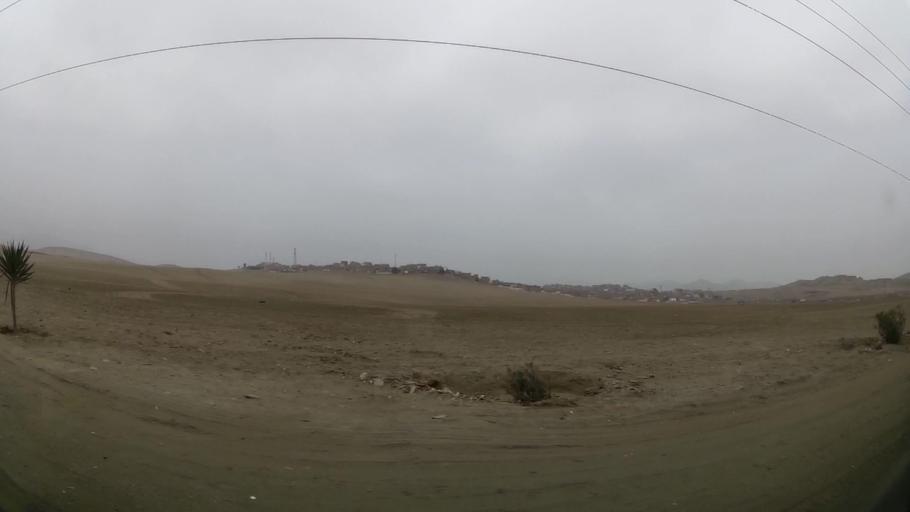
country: PE
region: Lima
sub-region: Lima
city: Punta Hermosa
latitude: -12.2510
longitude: -76.9057
